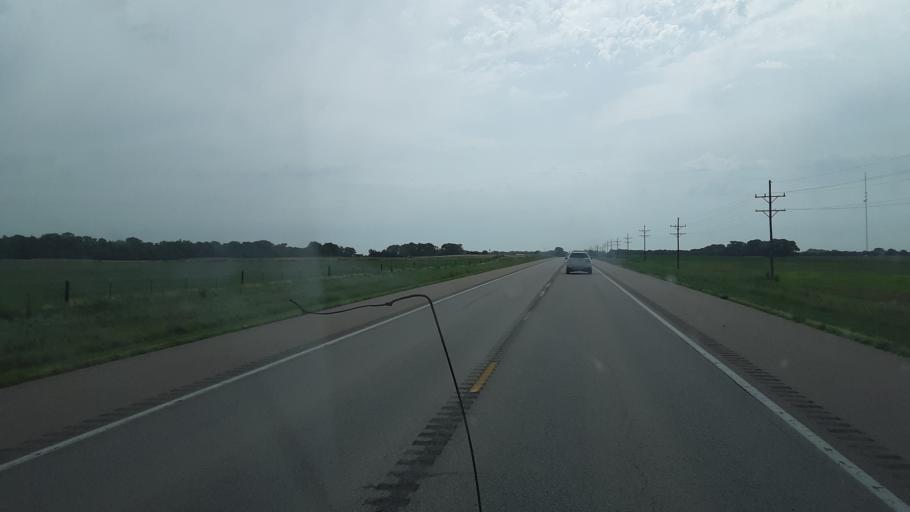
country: US
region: Kansas
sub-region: Stafford County
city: Stafford
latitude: 37.9552
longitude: -98.4479
